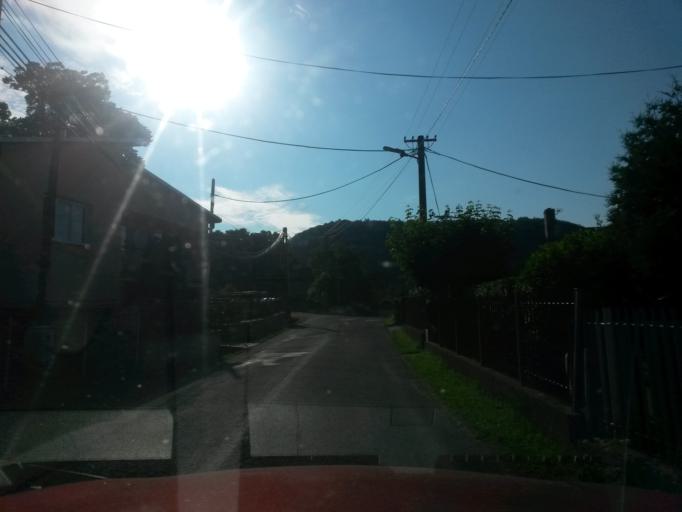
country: SK
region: Presovsky
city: Sabinov
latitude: 49.0860
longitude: 21.0264
